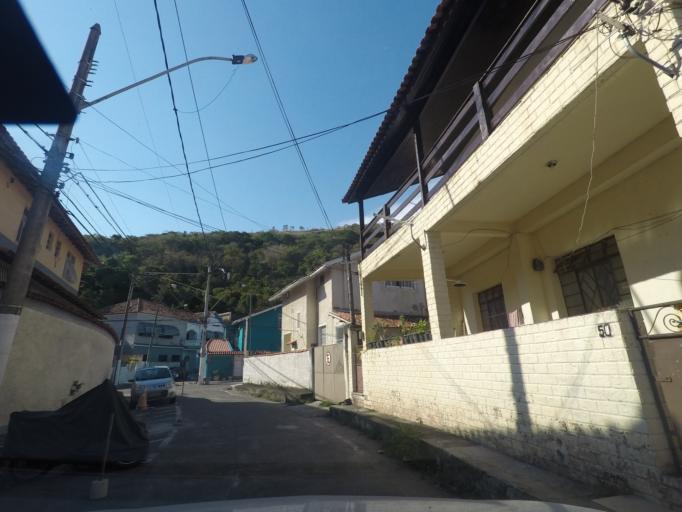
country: BR
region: Rio de Janeiro
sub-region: Niteroi
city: Niteroi
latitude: -22.8836
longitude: -43.1266
